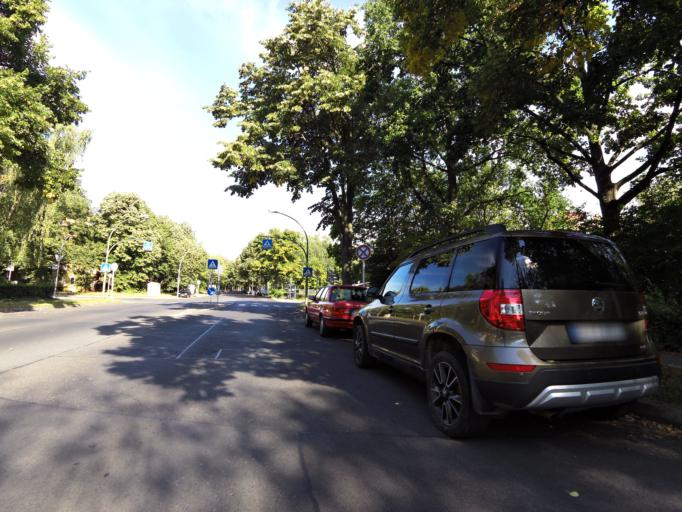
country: DE
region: Berlin
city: Zehlendorf Bezirk
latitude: 52.4331
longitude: 13.2764
